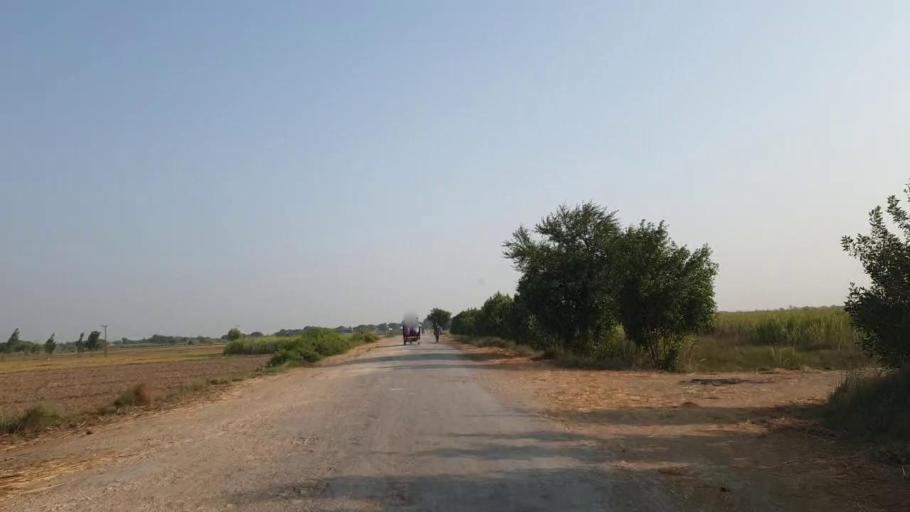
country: PK
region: Sindh
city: Bulri
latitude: 24.9921
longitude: 68.3859
